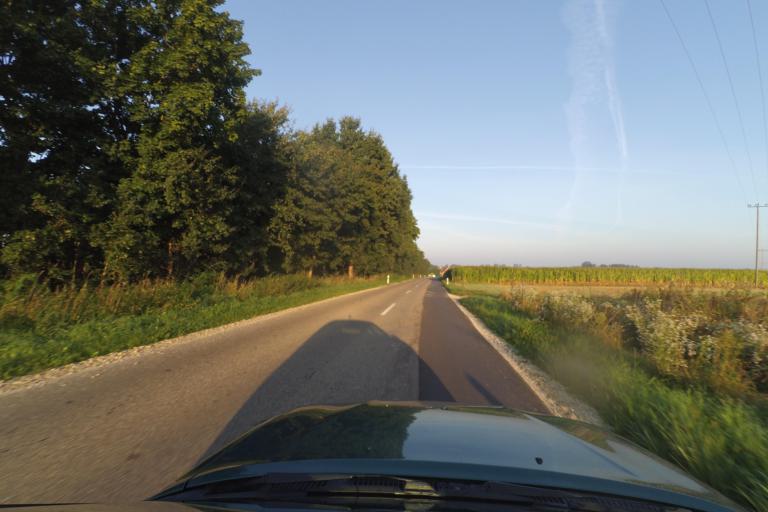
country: DE
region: Bavaria
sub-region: Upper Bavaria
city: Geisenfeld
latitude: 48.6804
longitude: 11.6376
